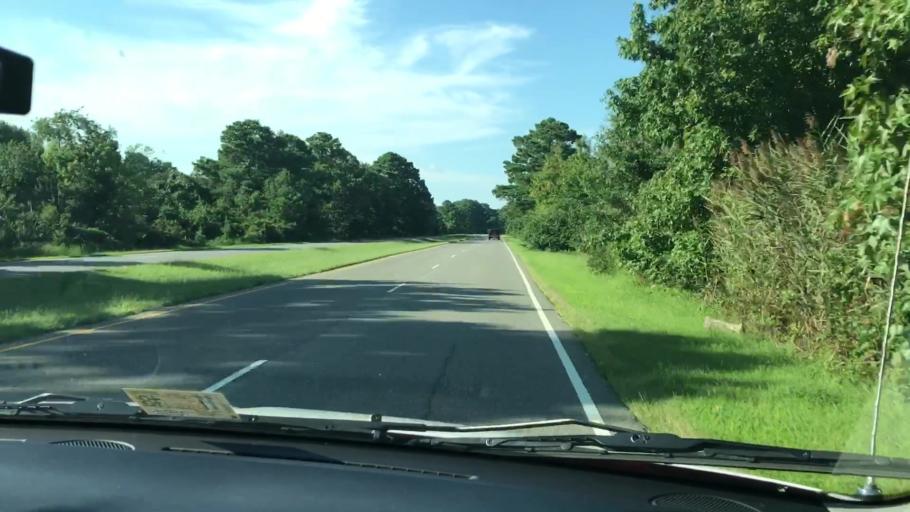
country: US
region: Virginia
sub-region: City of Hampton
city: Hampton
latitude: 37.0510
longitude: -76.3650
